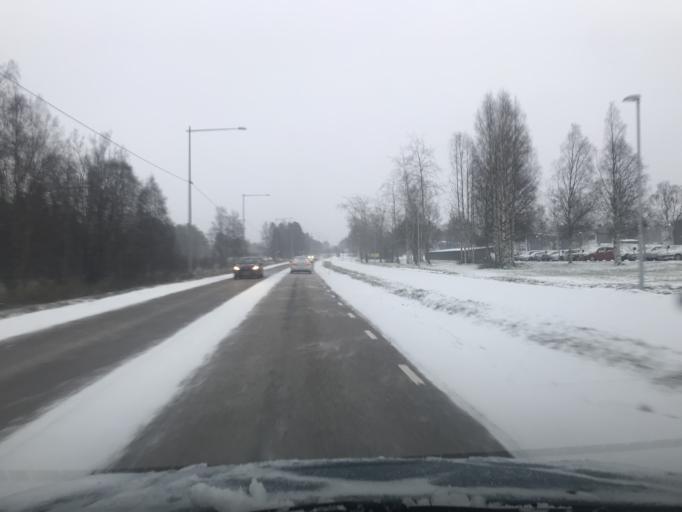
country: SE
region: Norrbotten
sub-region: Lulea Kommun
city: Gammelstad
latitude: 65.6368
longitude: 22.0276
